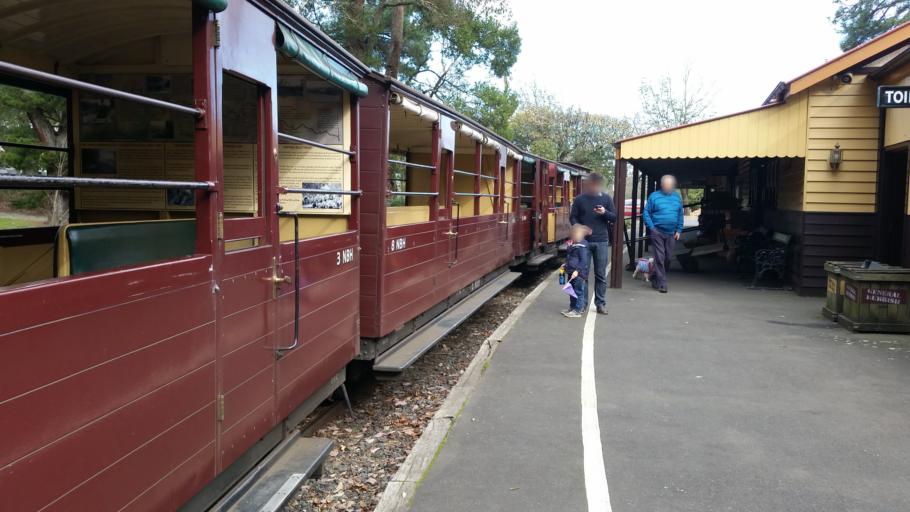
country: AU
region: Victoria
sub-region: Cardinia
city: Gembrook
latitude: -37.9518
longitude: 145.5496
